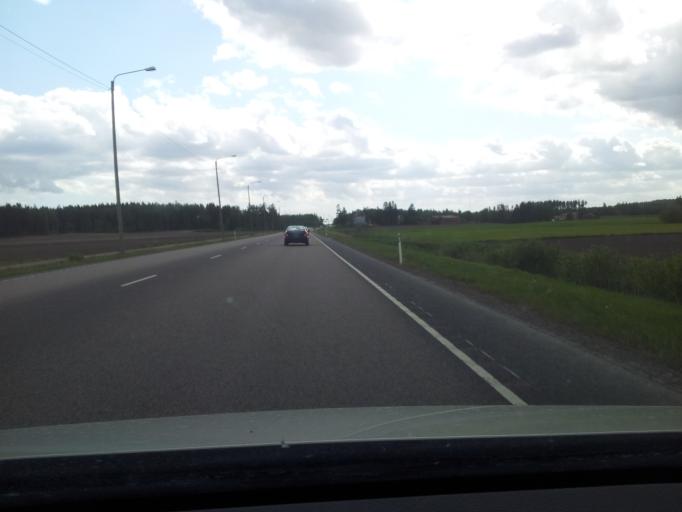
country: FI
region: Kymenlaakso
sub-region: Kouvola
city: Elimaeki
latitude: 60.8219
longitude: 26.5325
